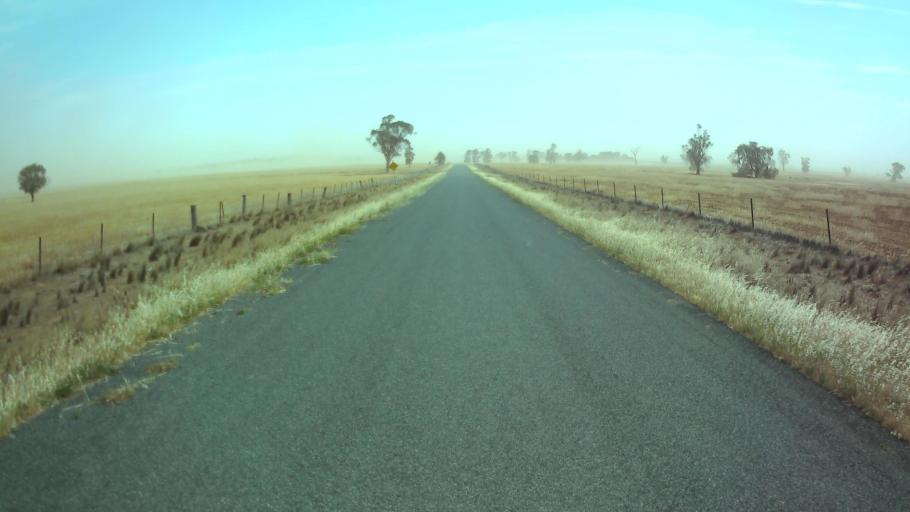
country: AU
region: New South Wales
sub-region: Weddin
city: Grenfell
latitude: -33.7430
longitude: 147.9923
